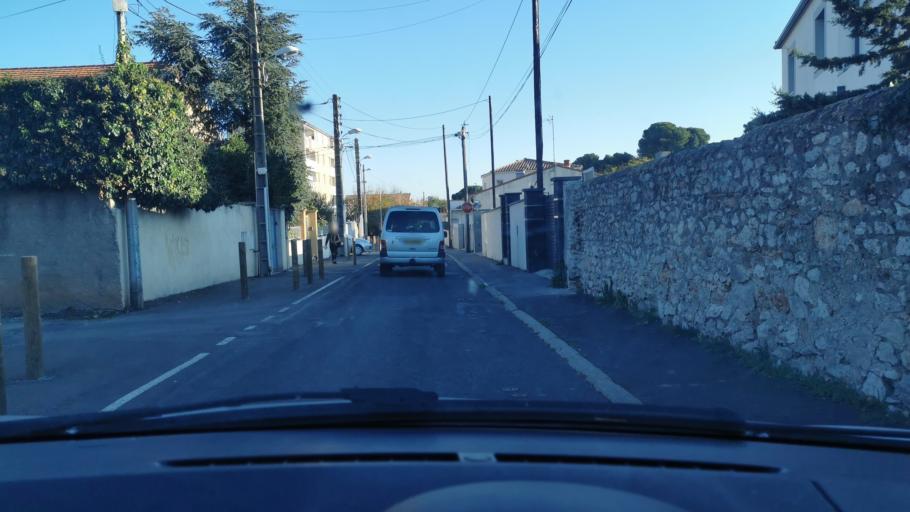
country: FR
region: Languedoc-Roussillon
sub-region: Departement de l'Herault
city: Frontignan
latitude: 43.4497
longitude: 3.7502
